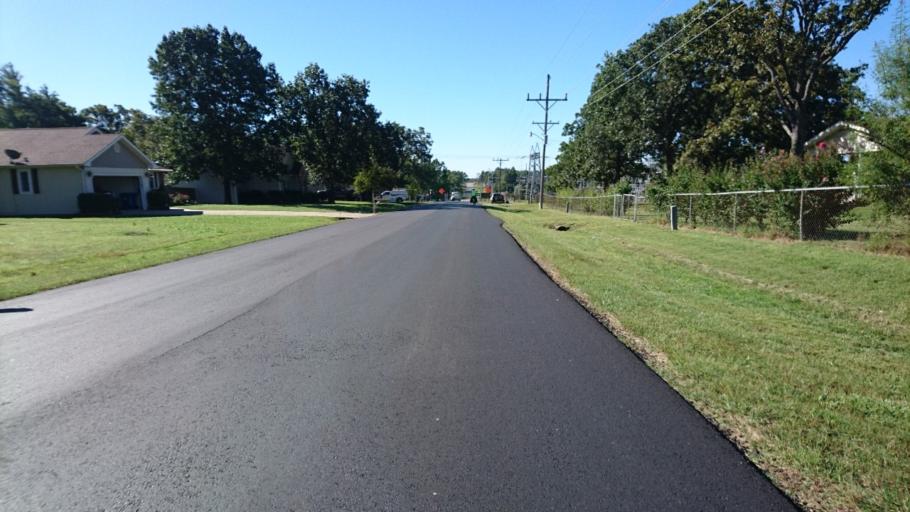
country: US
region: Missouri
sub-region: Jasper County
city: Joplin
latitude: 37.1158
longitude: -94.4939
